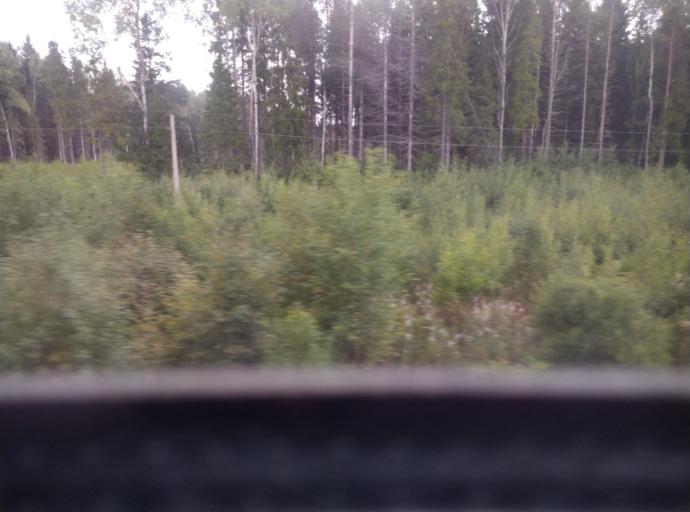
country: RU
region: Jaroslavl
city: Burmakino
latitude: 57.4366
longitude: 40.3390
